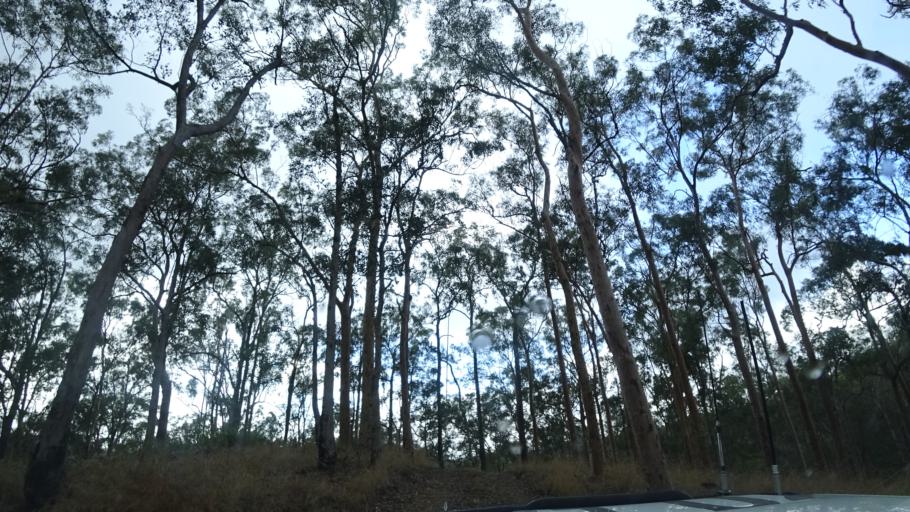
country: AU
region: Queensland
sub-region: Brisbane
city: Pullenvale
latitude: -27.4613
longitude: 152.8660
